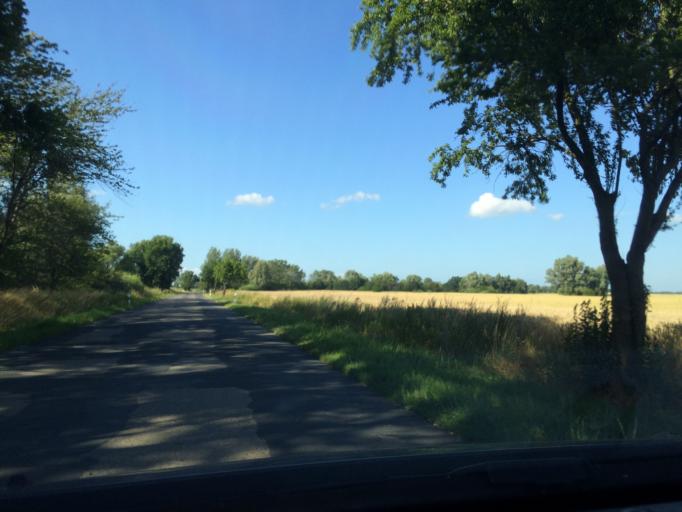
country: DE
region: Mecklenburg-Vorpommern
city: Niepars
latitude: 54.3585
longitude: 12.9056
